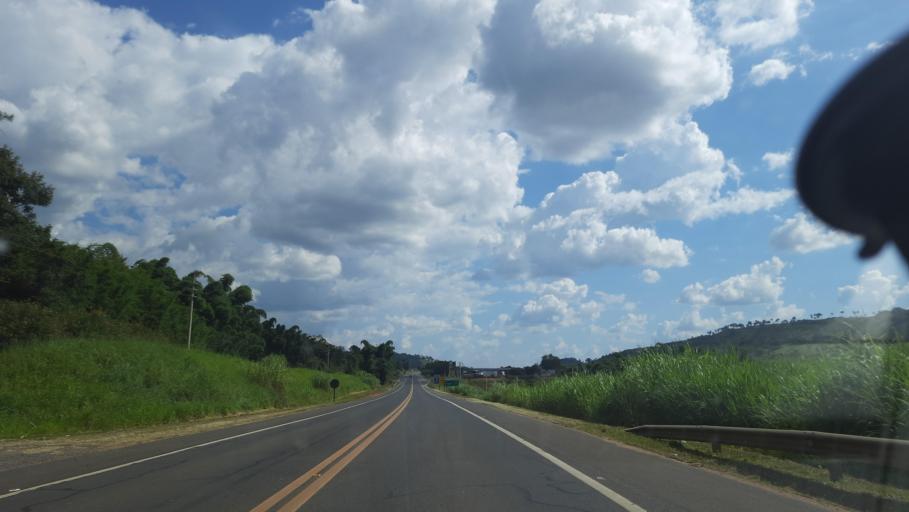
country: BR
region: Sao Paulo
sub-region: Sao Jose Do Rio Pardo
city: Sao Jose do Rio Pardo
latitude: -21.6331
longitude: -46.9027
